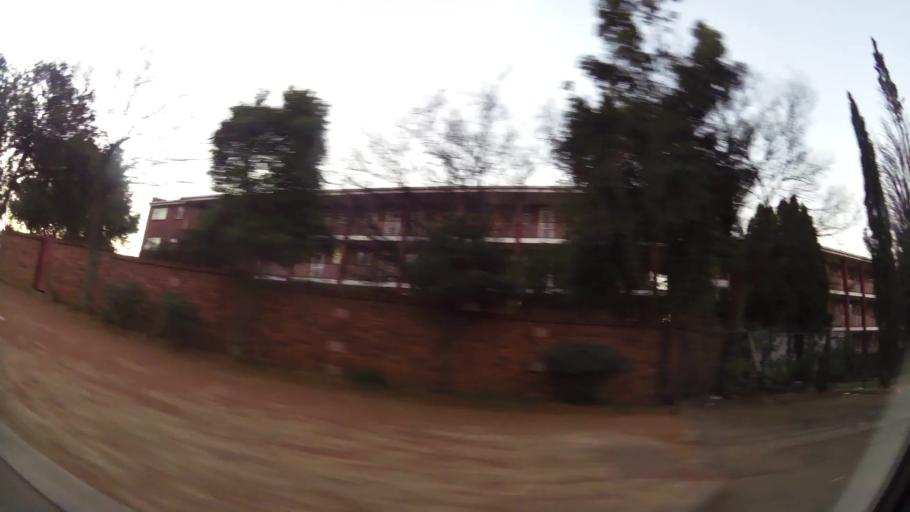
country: ZA
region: Gauteng
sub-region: Ekurhuleni Metropolitan Municipality
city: Germiston
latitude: -26.2630
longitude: 28.1655
